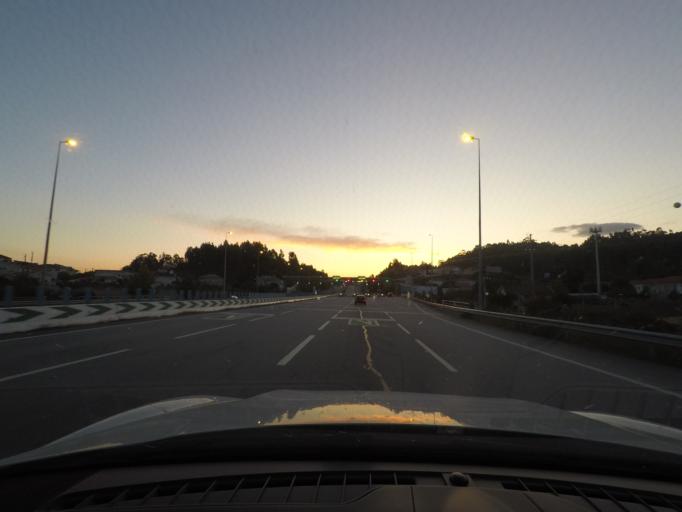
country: PT
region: Porto
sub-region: Lousada
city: Lousada
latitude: 41.2926
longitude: -8.2677
